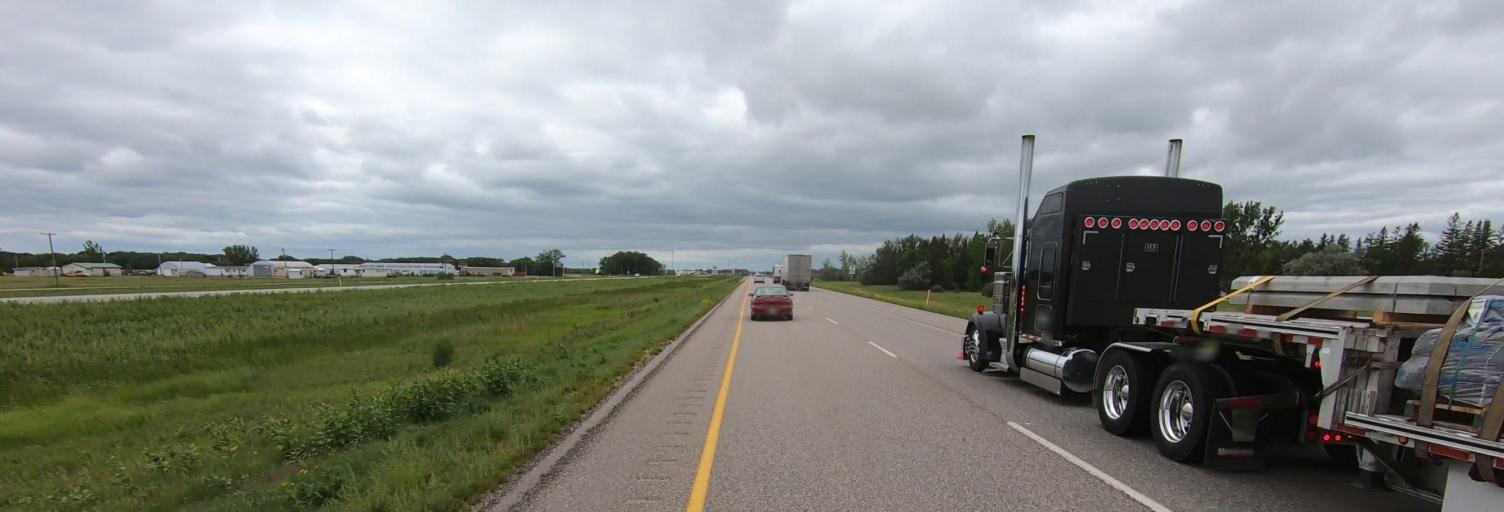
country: CA
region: Manitoba
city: Portage la Prairie
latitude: 49.9743
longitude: -98.1801
